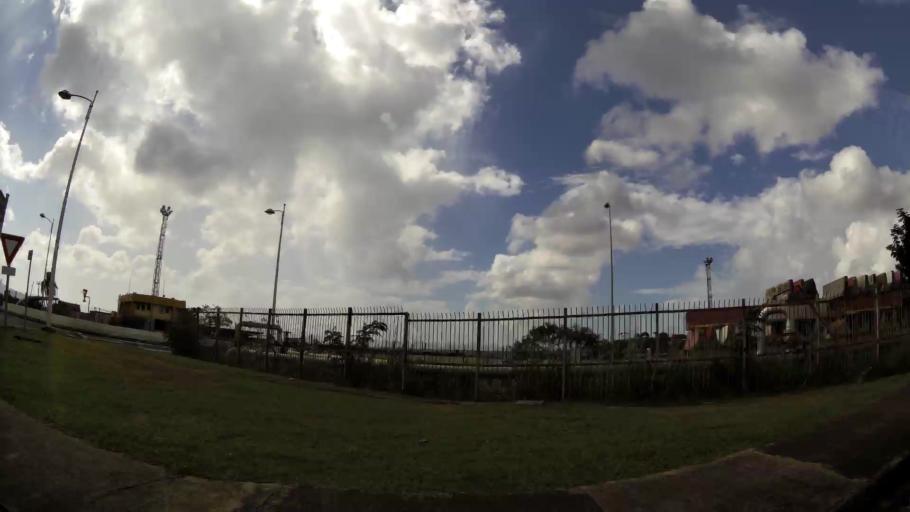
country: MQ
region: Martinique
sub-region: Martinique
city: Fort-de-France
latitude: 14.5961
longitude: -61.0591
